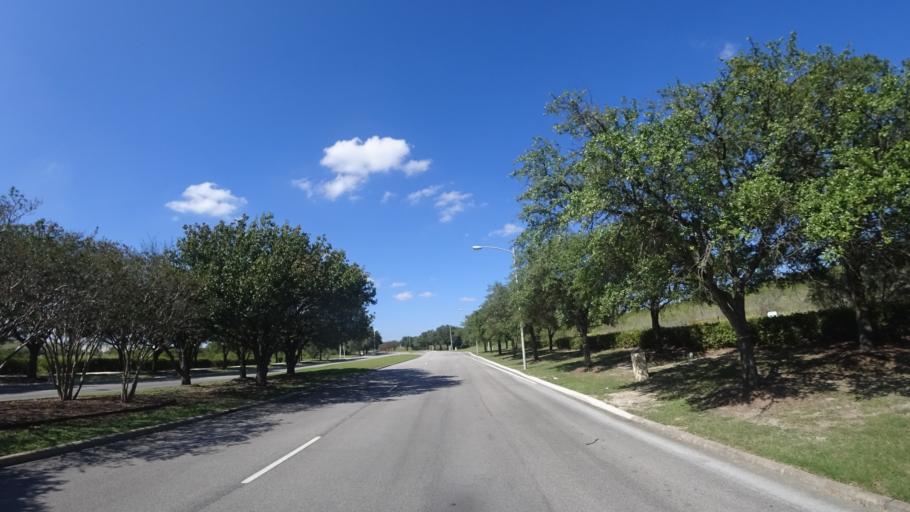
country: US
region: Texas
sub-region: Travis County
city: Manor
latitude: 30.3361
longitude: -97.6079
